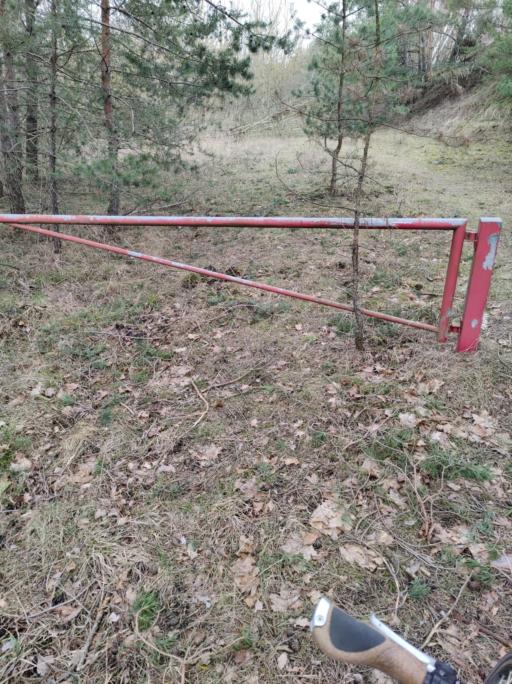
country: DE
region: Brandenburg
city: Wildau
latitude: 52.3206
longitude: 13.6603
